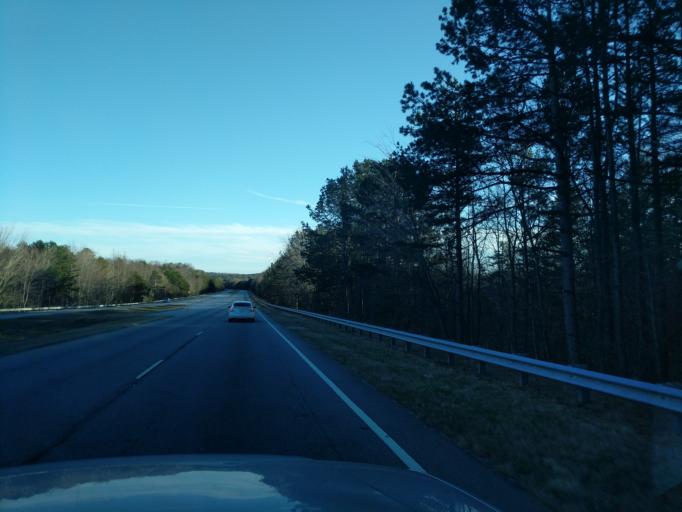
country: US
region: Georgia
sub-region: Stephens County
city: Toccoa
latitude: 34.5737
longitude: -83.4038
